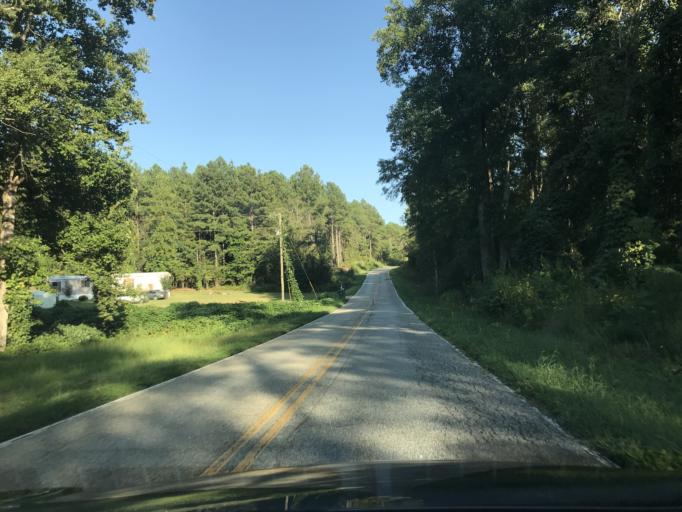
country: US
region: South Carolina
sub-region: Spartanburg County
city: Mayo
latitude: 35.1076
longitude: -81.7806
